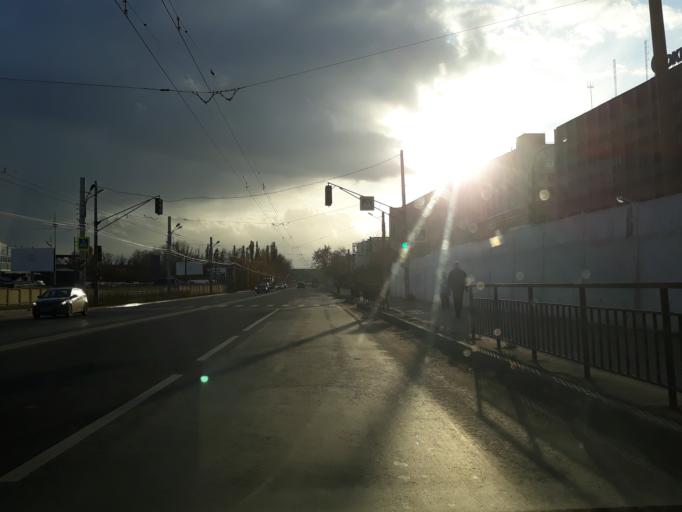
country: RU
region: Nizjnij Novgorod
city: Nizhniy Novgorod
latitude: 56.3205
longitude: 43.9072
